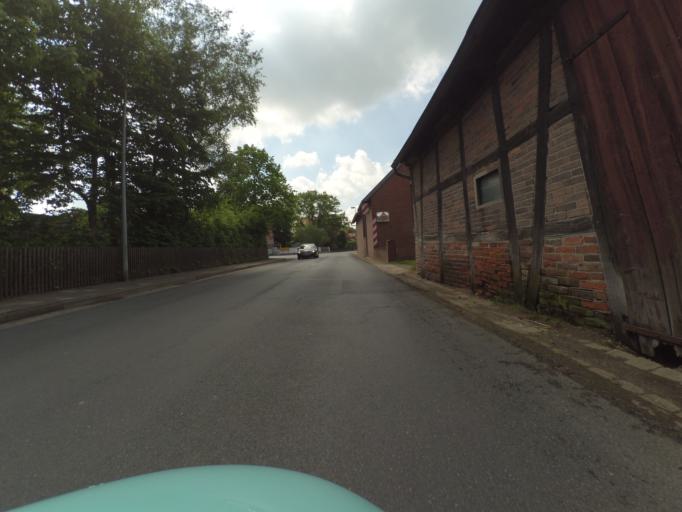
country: DE
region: Lower Saxony
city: Didderse
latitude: 52.3858
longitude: 10.3549
